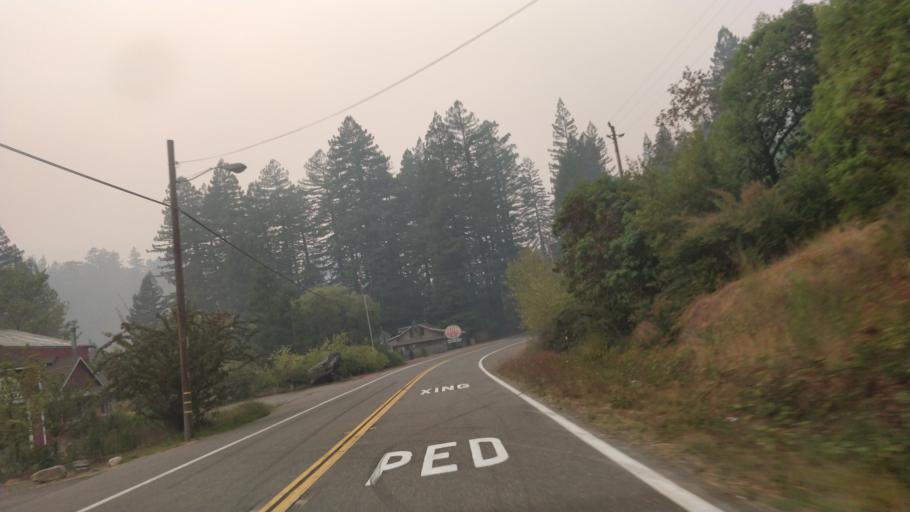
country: US
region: California
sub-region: Humboldt County
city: Redway
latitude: 40.2674
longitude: -123.8739
